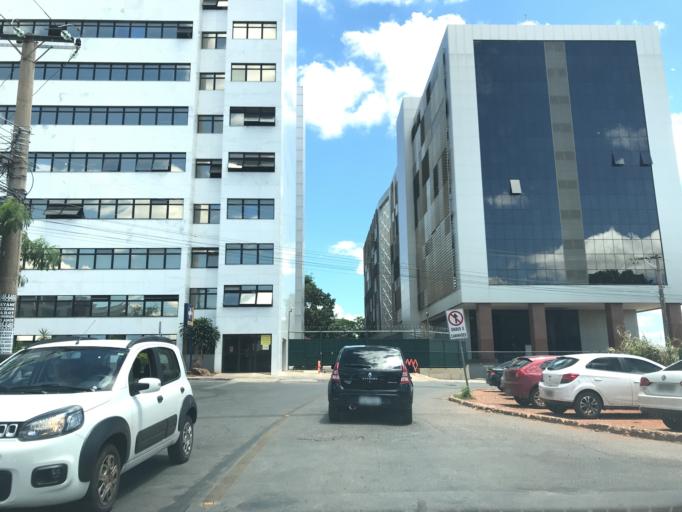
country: BR
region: Federal District
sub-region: Brasilia
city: Brasilia
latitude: -15.7887
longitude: -47.9086
